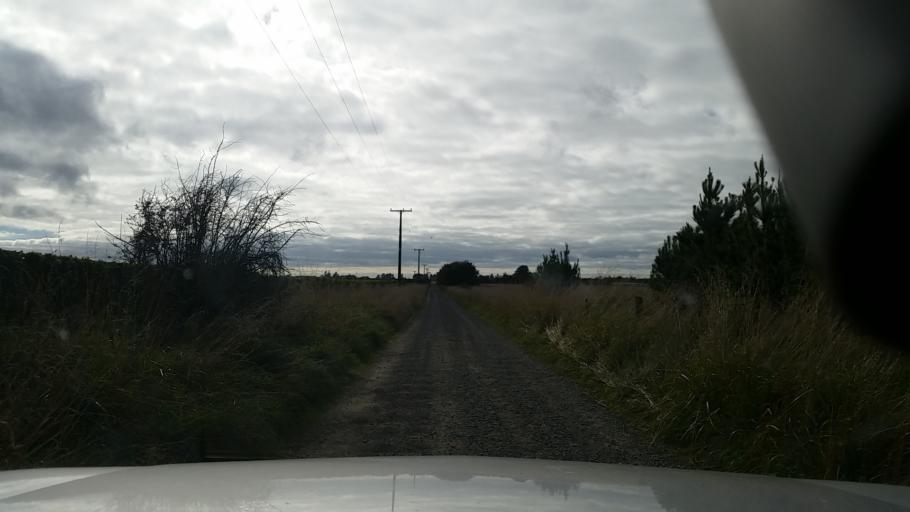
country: NZ
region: Marlborough
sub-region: Marlborough District
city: Blenheim
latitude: -41.4665
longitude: 173.9843
